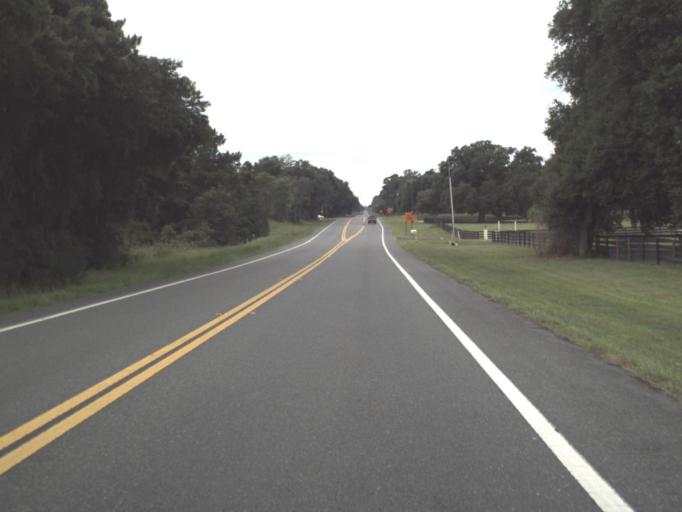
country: US
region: Florida
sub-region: Levy County
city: Williston
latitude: 29.3040
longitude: -82.4494
